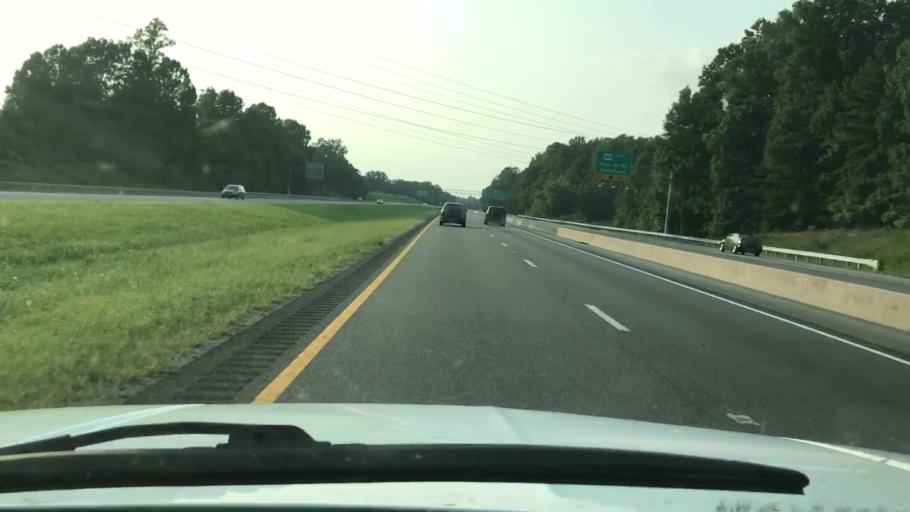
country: US
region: Virginia
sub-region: Chesterfield County
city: Brandermill
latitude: 37.4180
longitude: -77.6243
